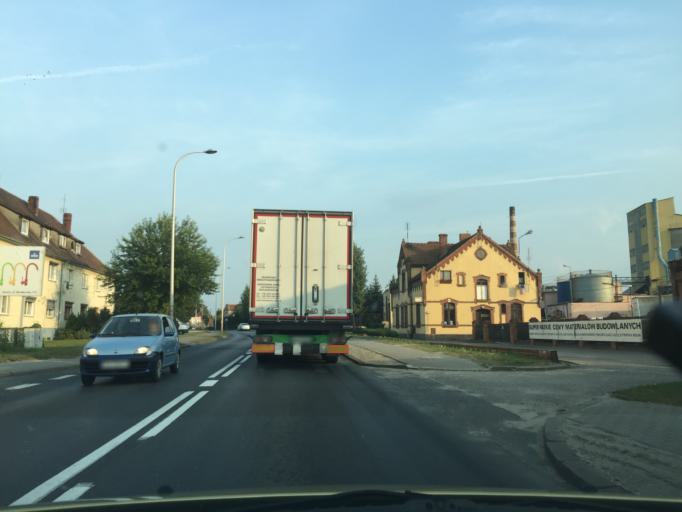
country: PL
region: Greater Poland Voivodeship
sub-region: Powiat jarocinski
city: Jarocin
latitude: 51.9768
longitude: 17.4915
